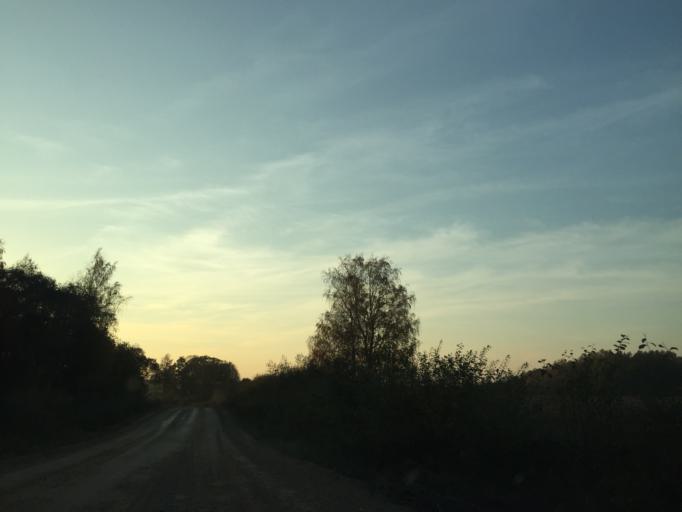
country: LV
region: Priekule
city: Priekule
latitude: 56.4729
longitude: 21.6120
